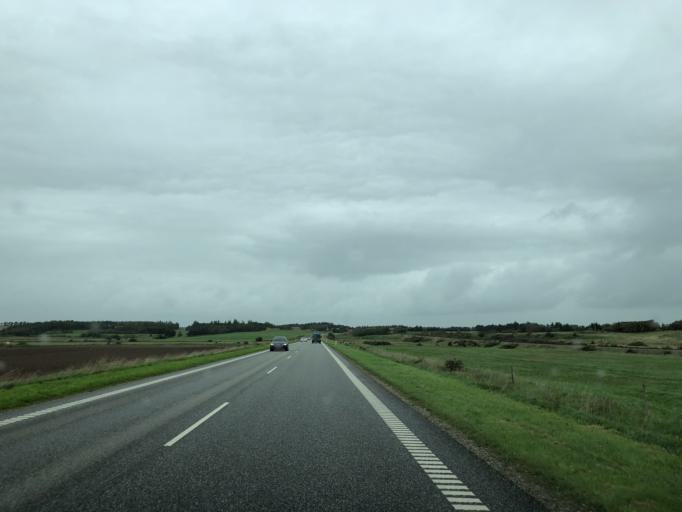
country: DK
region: Central Jutland
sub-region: Struer Kommune
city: Struer
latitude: 56.5921
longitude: 8.5262
